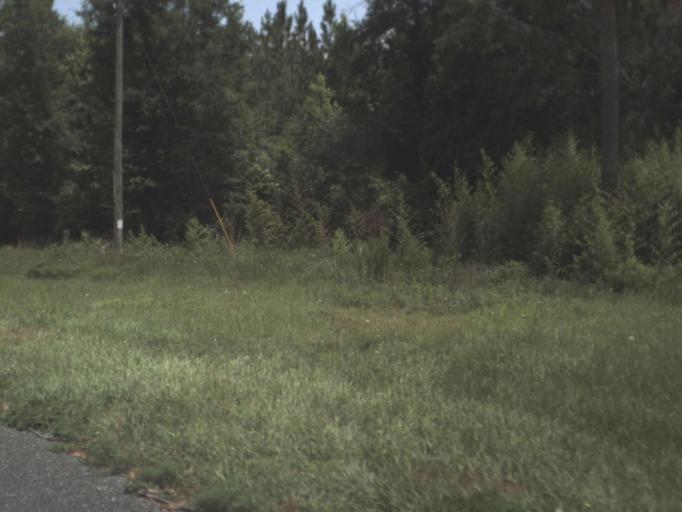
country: US
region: Florida
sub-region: Taylor County
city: Perry
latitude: 29.9763
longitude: -83.4853
